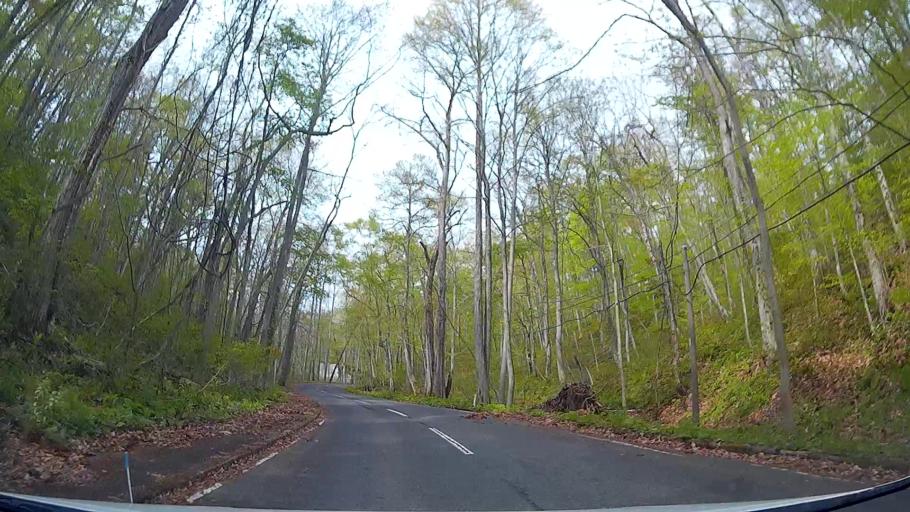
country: JP
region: Akita
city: Hanawa
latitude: 40.4268
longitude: 140.9121
